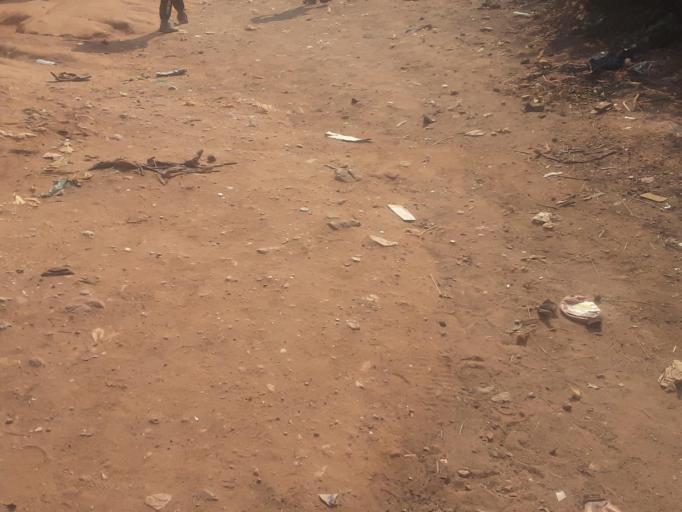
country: ZM
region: Lusaka
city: Lusaka
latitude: -15.3572
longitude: 28.2943
